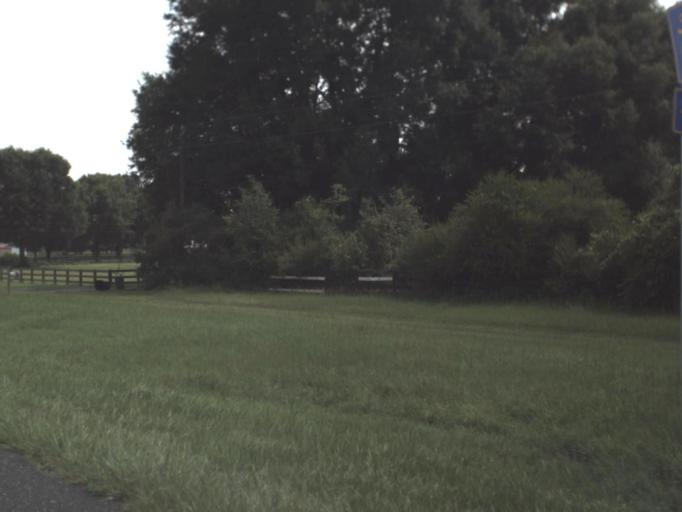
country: US
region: Florida
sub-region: Alachua County
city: High Springs
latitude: 29.8858
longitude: -82.6090
